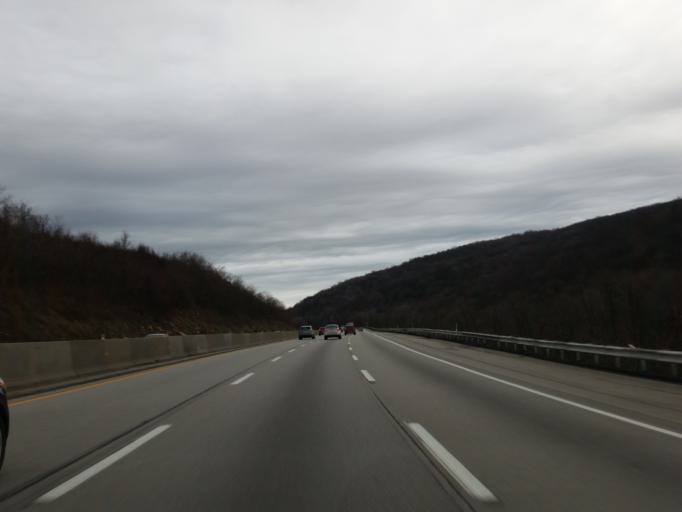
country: US
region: Pennsylvania
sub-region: Westmoreland County
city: Ligonier
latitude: 40.1166
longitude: -79.2611
